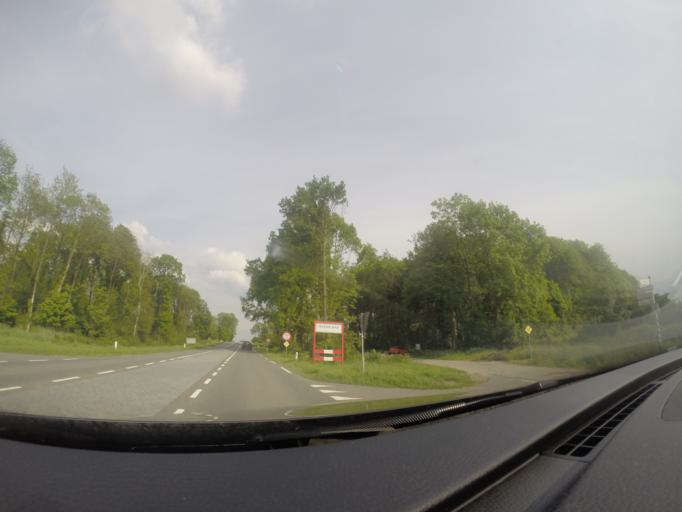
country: NL
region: Flevoland
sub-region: Gemeente Noordoostpolder
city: Ens
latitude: 52.6380
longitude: 5.7706
